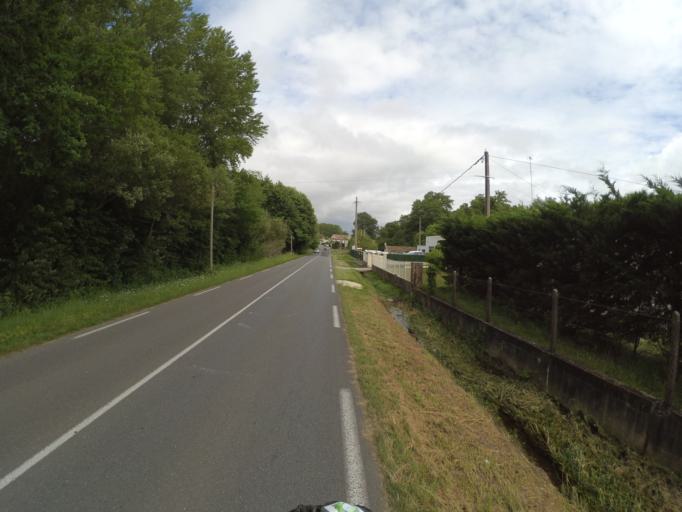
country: FR
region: Aquitaine
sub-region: Departement de la Gironde
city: Soussans
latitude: 45.0557
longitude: -0.7065
